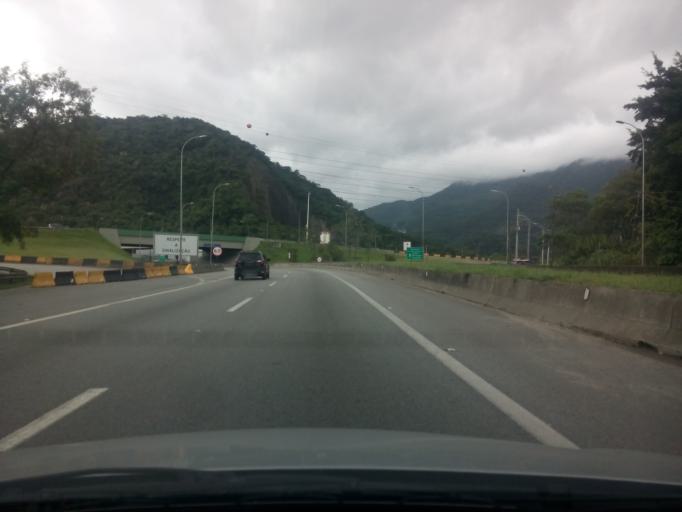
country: BR
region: Sao Paulo
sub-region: Cubatao
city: Cubatao
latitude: -23.8877
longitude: -46.4388
